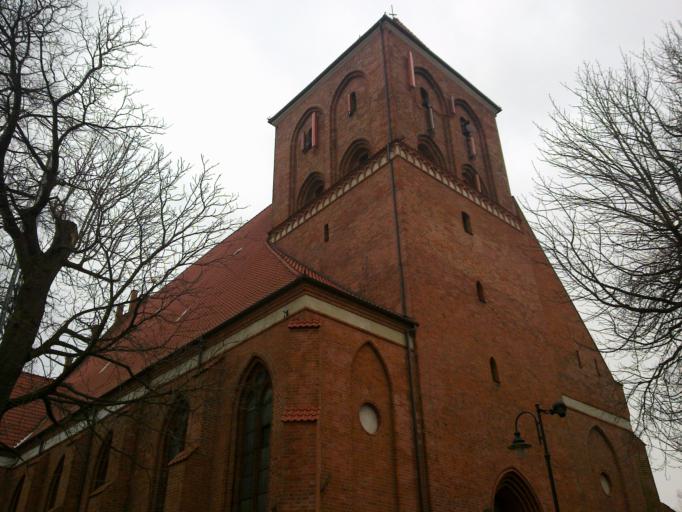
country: PL
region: Pomeranian Voivodeship
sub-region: Powiat pucki
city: Puck
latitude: 54.7217
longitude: 18.4108
